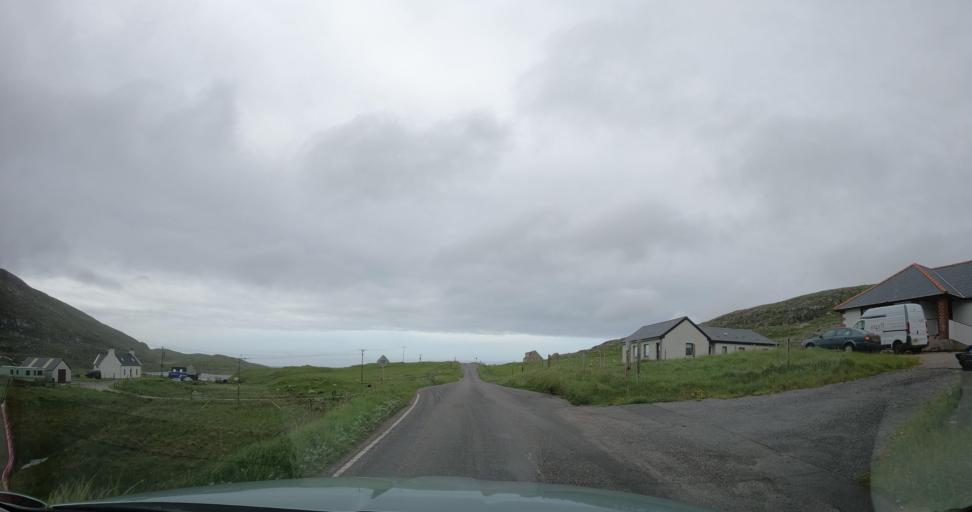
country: GB
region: Scotland
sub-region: Eilean Siar
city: Barra
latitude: 56.9646
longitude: -7.5116
